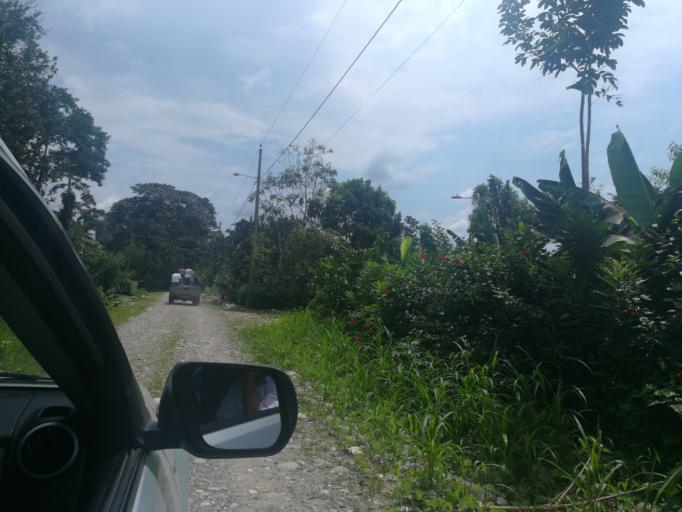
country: EC
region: Napo
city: Tena
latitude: -1.0299
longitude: -77.6781
